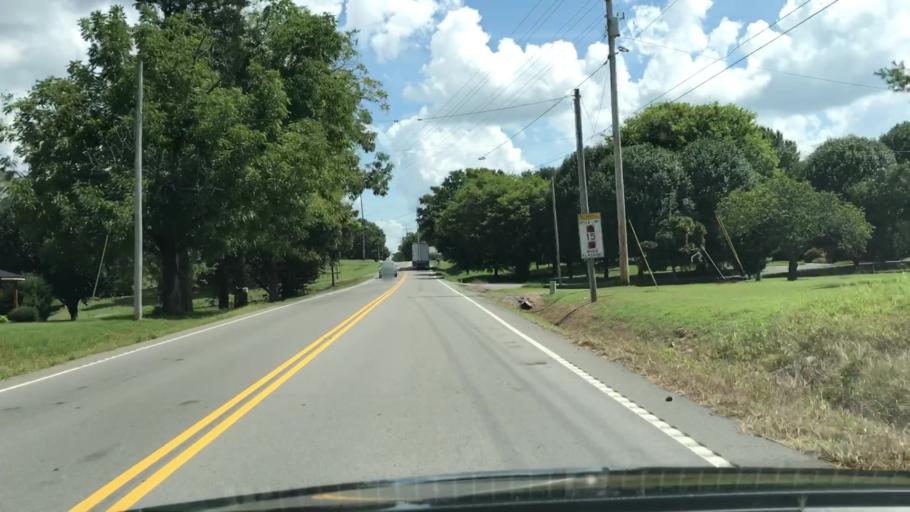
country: US
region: Tennessee
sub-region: Robertson County
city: Cross Plains
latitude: 36.5494
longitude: -86.7051
